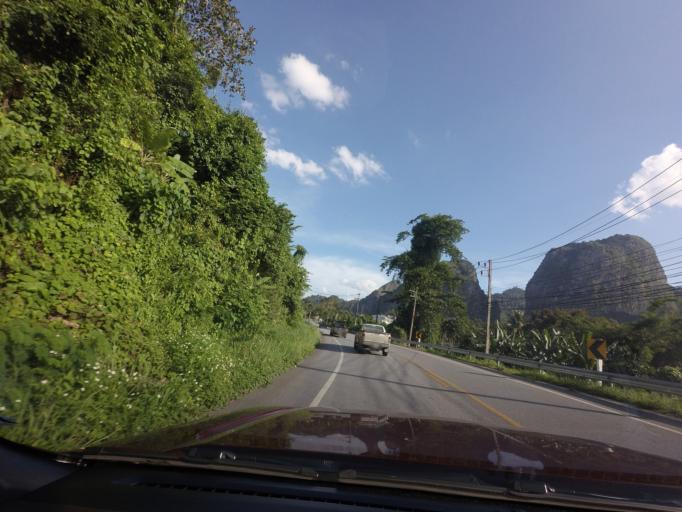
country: TH
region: Yala
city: Than To
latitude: 6.2240
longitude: 101.1651
